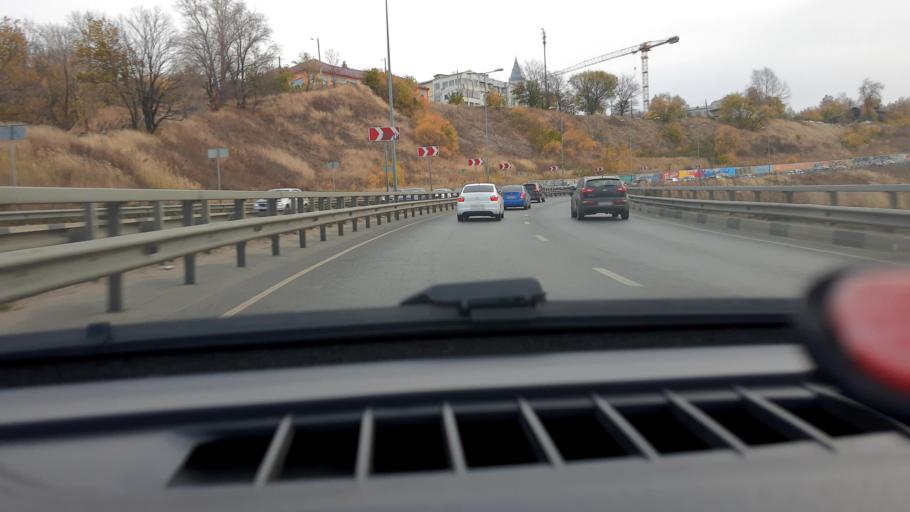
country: RU
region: Nizjnij Novgorod
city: Nizhniy Novgorod
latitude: 56.3162
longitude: 43.9723
